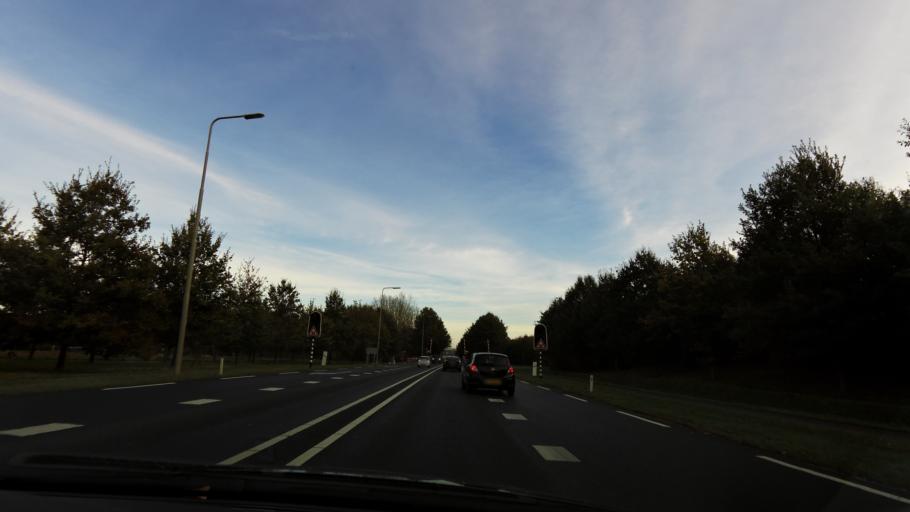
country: NL
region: Limburg
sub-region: Gemeente Sittard-Geleen
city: Limbricht
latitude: 51.0102
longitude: 5.8468
